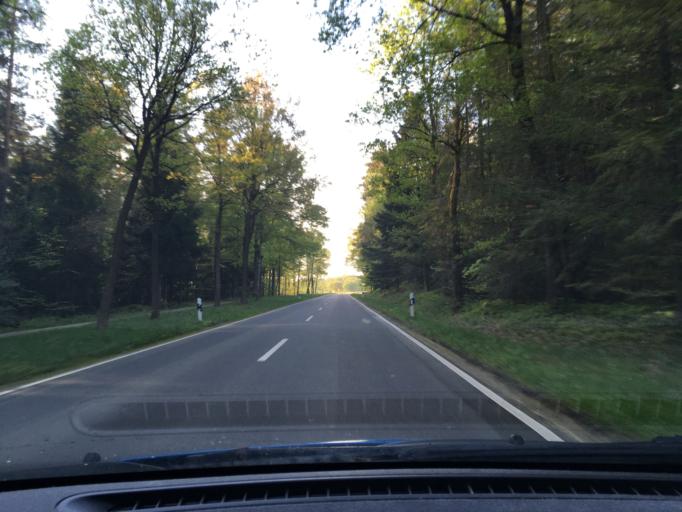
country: DE
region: Lower Saxony
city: Wietzendorf
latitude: 52.8821
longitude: 9.9837
